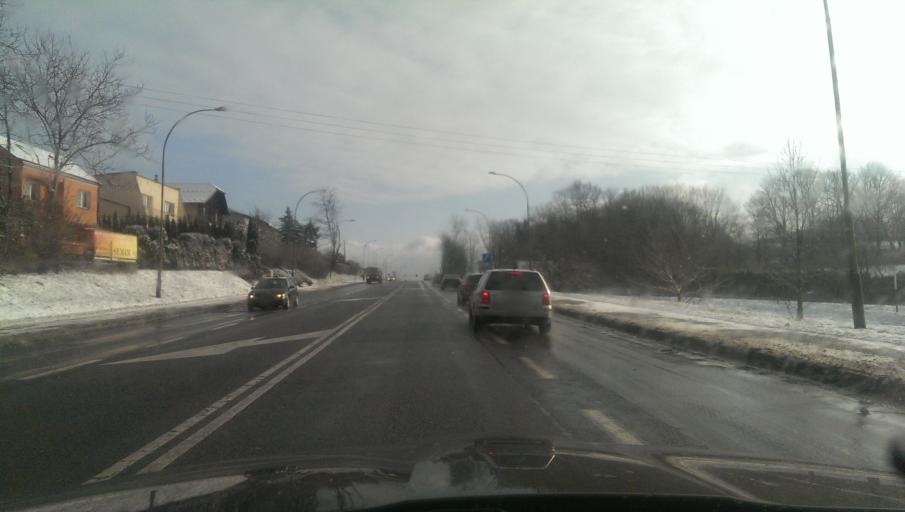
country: PL
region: Subcarpathian Voivodeship
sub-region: Powiat sanocki
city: Sanok
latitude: 49.5654
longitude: 22.1770
